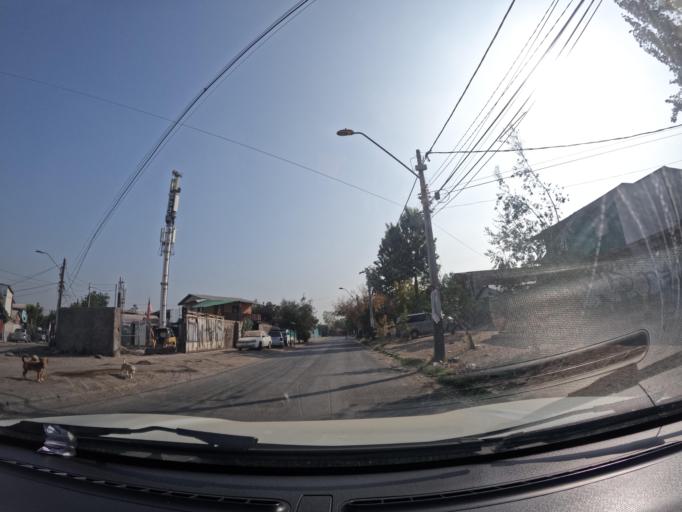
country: CL
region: Santiago Metropolitan
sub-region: Provincia de Santiago
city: Villa Presidente Frei, Nunoa, Santiago, Chile
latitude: -33.4766
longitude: -70.5678
